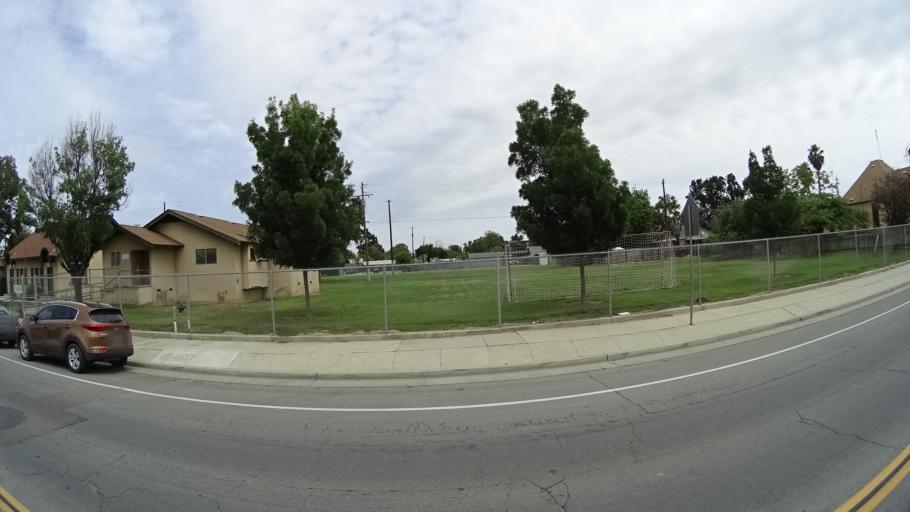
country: US
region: California
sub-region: Kings County
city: Hanford
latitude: 36.3348
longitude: -119.6436
